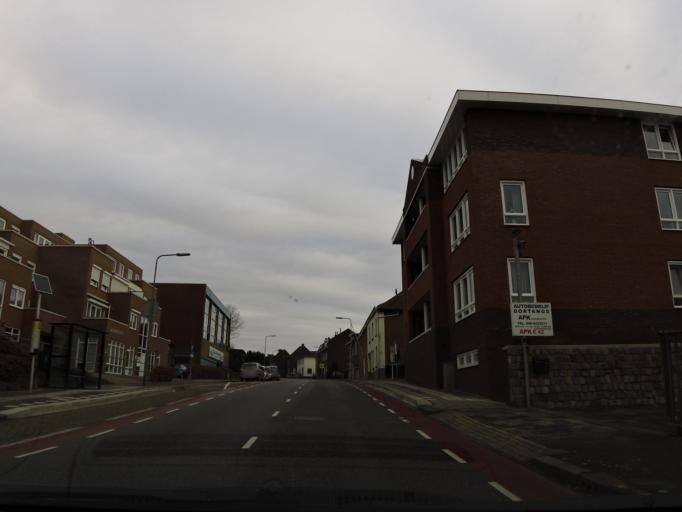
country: NL
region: Limburg
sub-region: Gemeente Schinnen
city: Schinnen
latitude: 50.9423
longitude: 5.8885
